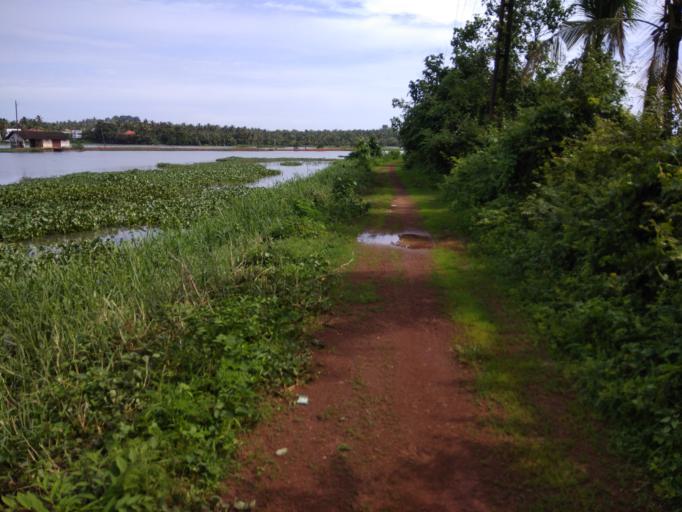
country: IN
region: Kerala
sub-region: Thrissur District
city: Trichur
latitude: 10.5328
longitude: 76.1775
